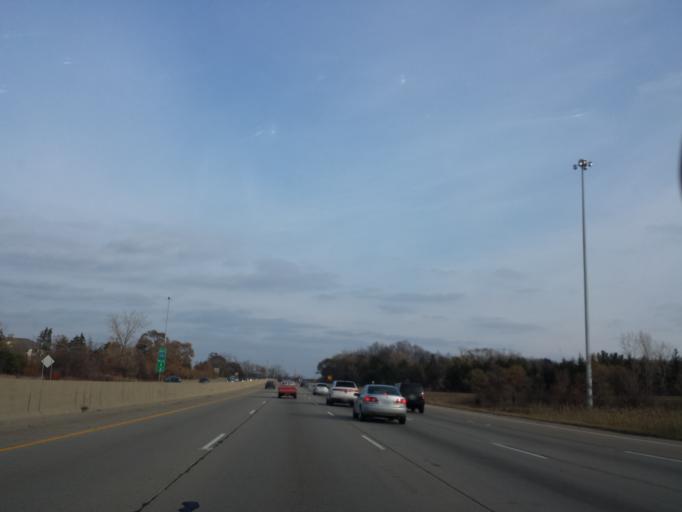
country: US
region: Michigan
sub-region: Oakland County
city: Farmington Hills
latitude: 42.4960
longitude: -83.3578
